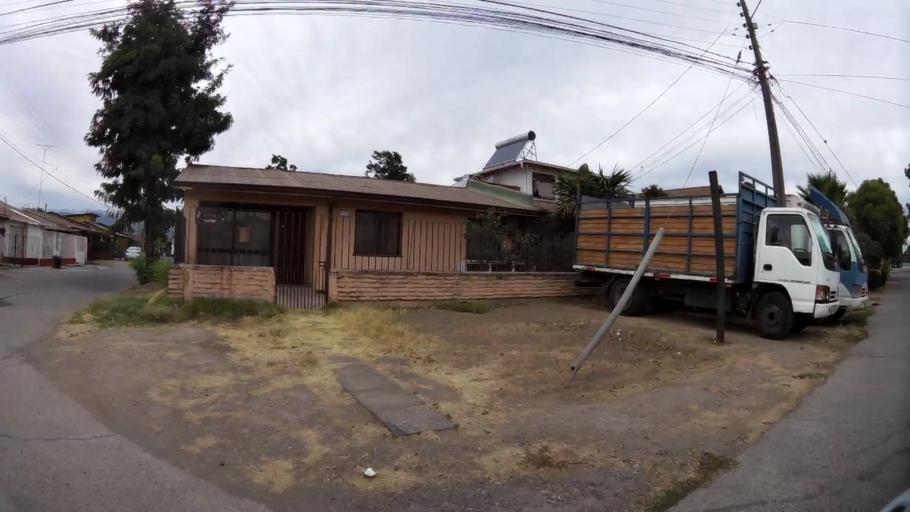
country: CL
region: O'Higgins
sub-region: Provincia de Cachapoal
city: Rancagua
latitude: -34.1531
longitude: -70.7424
